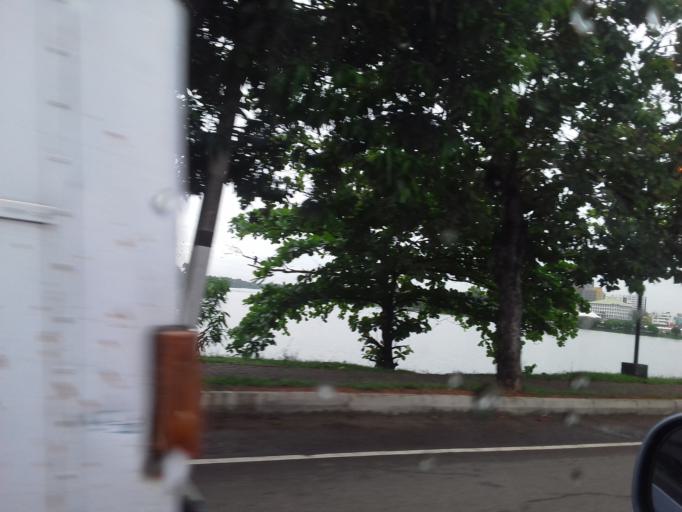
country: LK
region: Western
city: Battaramulla South
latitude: 6.9049
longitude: 79.9060
